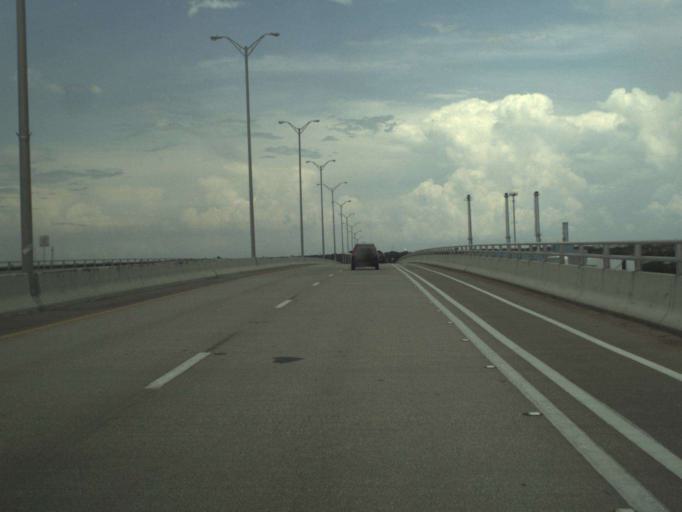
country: US
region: Florida
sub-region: Indian River County
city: Vero Beach
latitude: 27.6324
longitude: -80.3704
